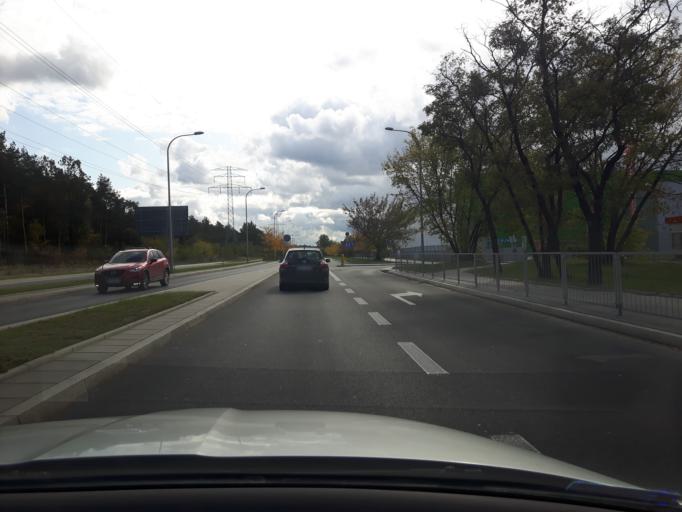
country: PL
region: Masovian Voivodeship
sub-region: Warszawa
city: Rembertow
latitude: 52.2424
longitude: 21.1393
